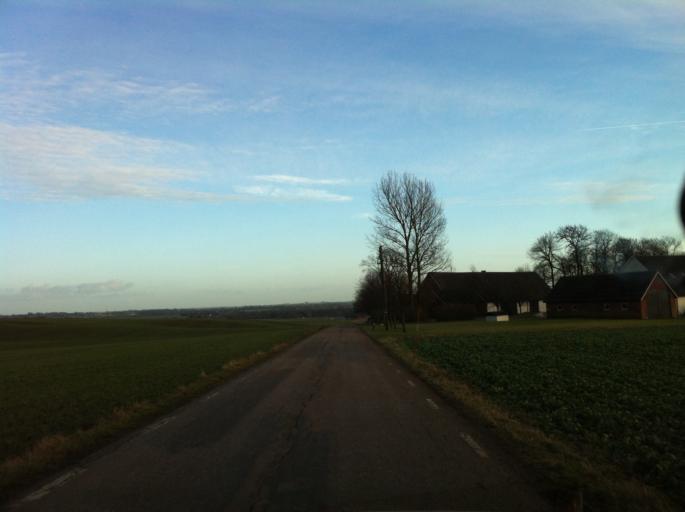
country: SE
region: Skane
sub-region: Landskrona
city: Asmundtorp
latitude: 55.8994
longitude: 12.9265
